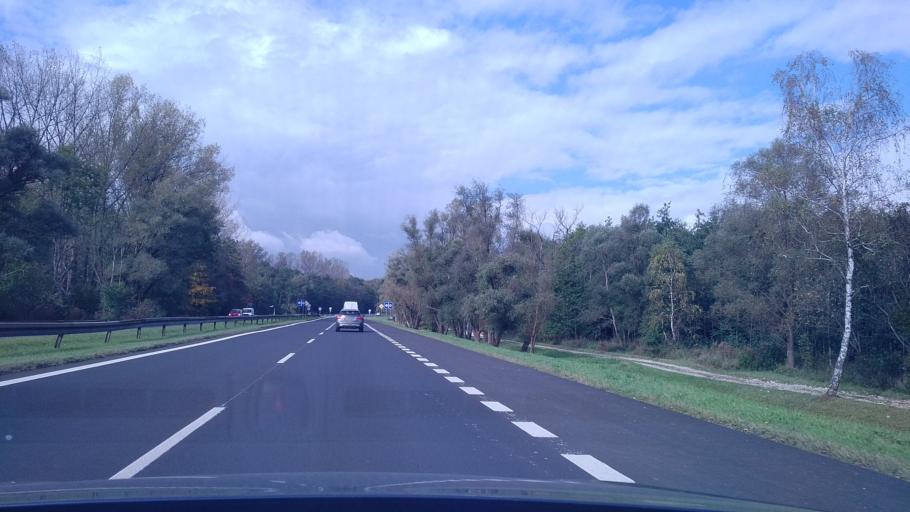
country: PL
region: Lesser Poland Voivodeship
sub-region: Powiat krakowski
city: Modlniczka
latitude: 50.1061
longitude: 19.8821
